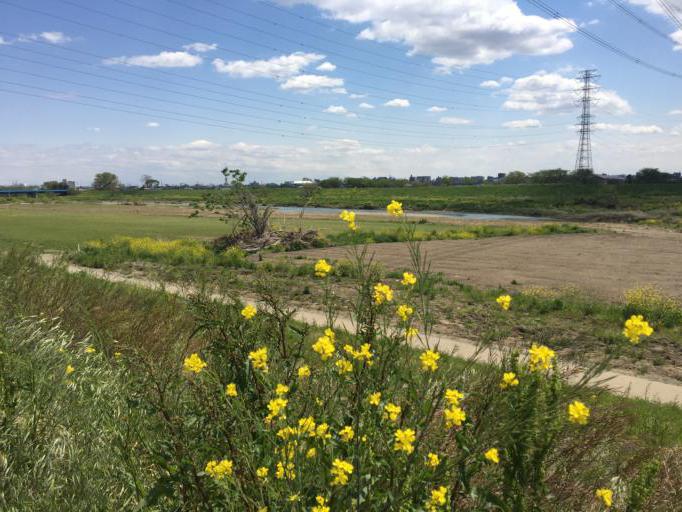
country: JP
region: Saitama
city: Kawagoe
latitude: 35.9317
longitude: 139.4561
